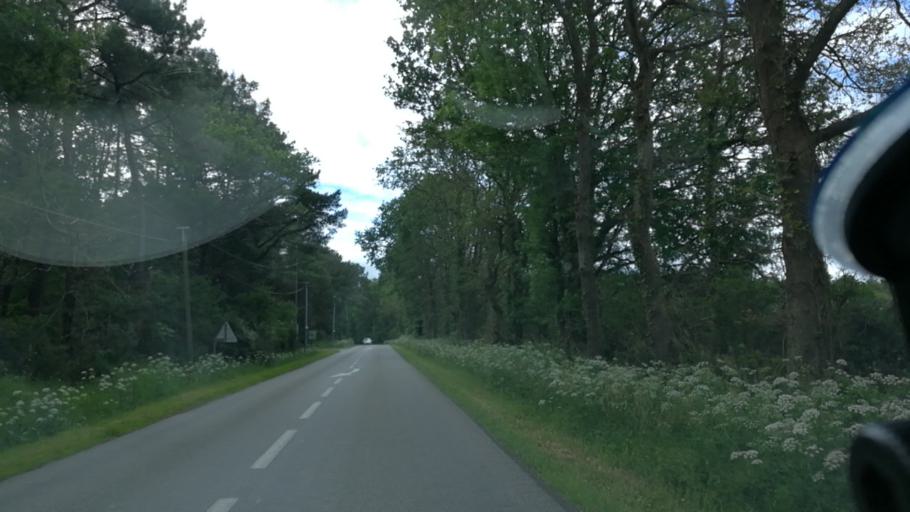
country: FR
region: Brittany
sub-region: Departement du Morbihan
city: Penestin
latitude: 47.4773
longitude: -2.4341
